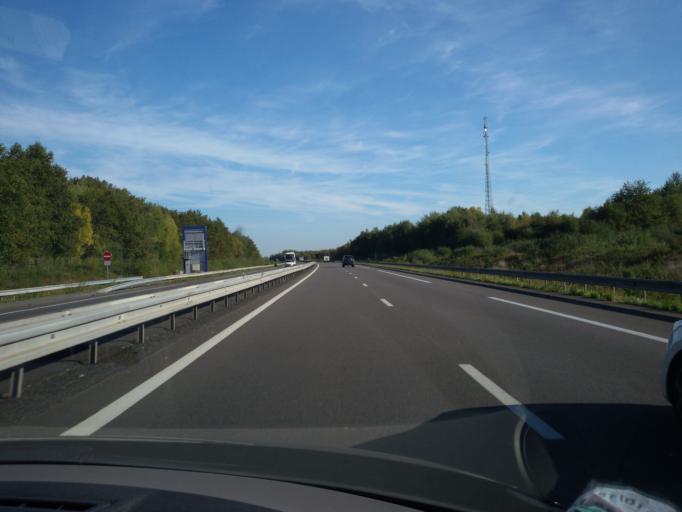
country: FR
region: Centre
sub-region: Departement du Loir-et-Cher
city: Salbris
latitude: 47.3726
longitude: 2.0537
